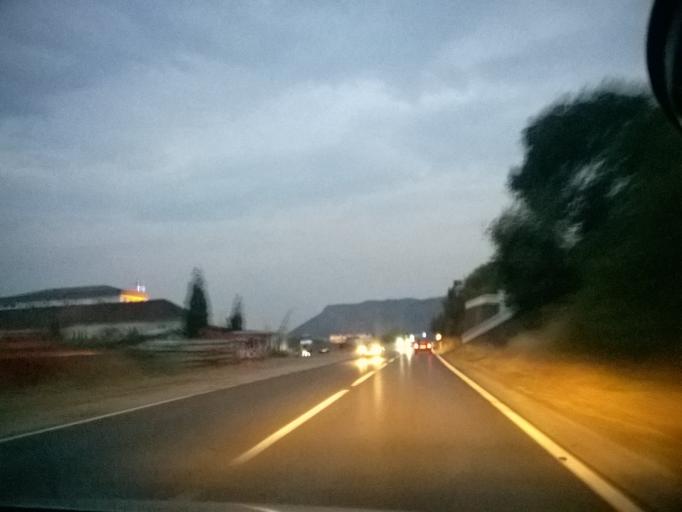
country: ME
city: Spuz
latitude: 42.4764
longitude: 19.1709
